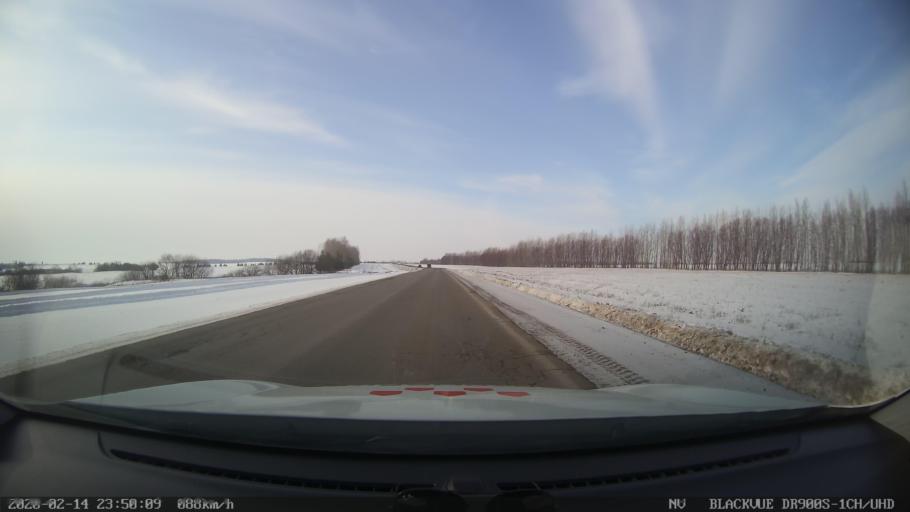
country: RU
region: Tatarstan
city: Kuybyshevskiy Zaton
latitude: 55.2580
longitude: 49.1671
